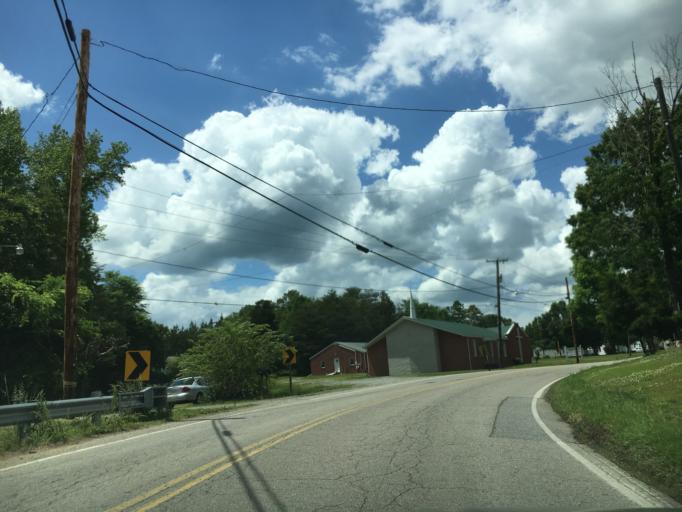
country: US
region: Virginia
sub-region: Halifax County
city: South Boston
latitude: 36.6988
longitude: -78.9224
